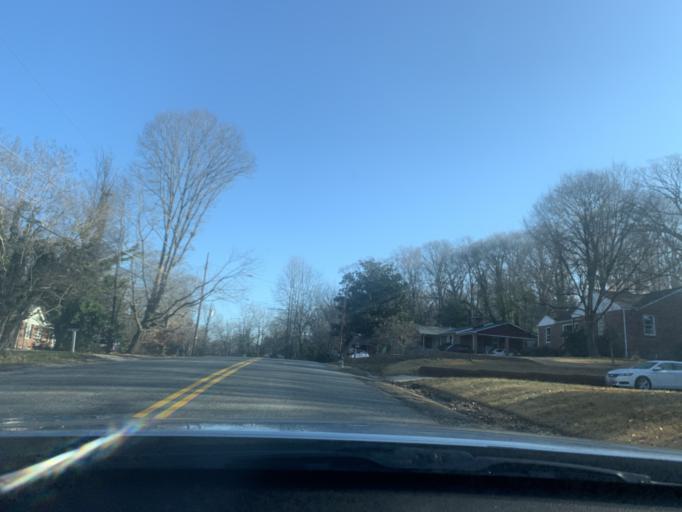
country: US
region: Maryland
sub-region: Prince George's County
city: Camp Springs
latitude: 38.8145
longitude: -76.9215
